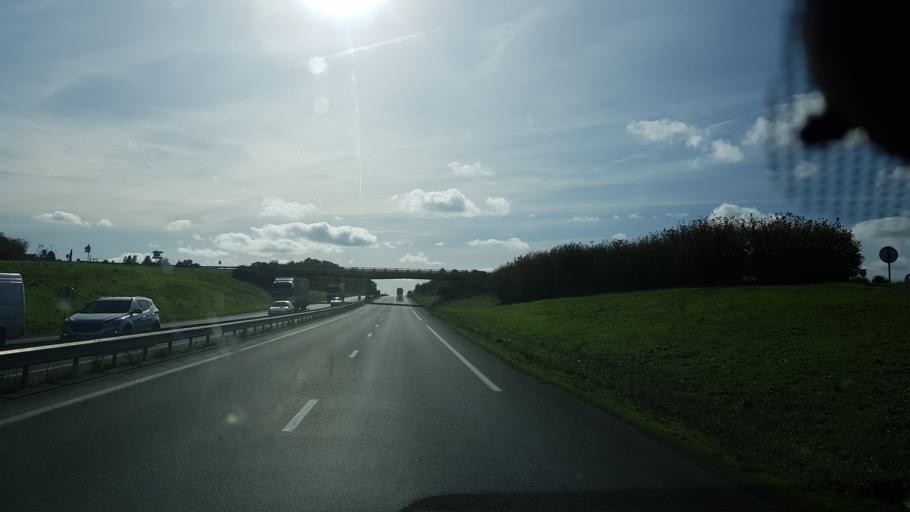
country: FR
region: Poitou-Charentes
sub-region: Departement de la Charente
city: Chasseneuil-sur-Bonnieure
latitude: 45.8138
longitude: 0.4517
